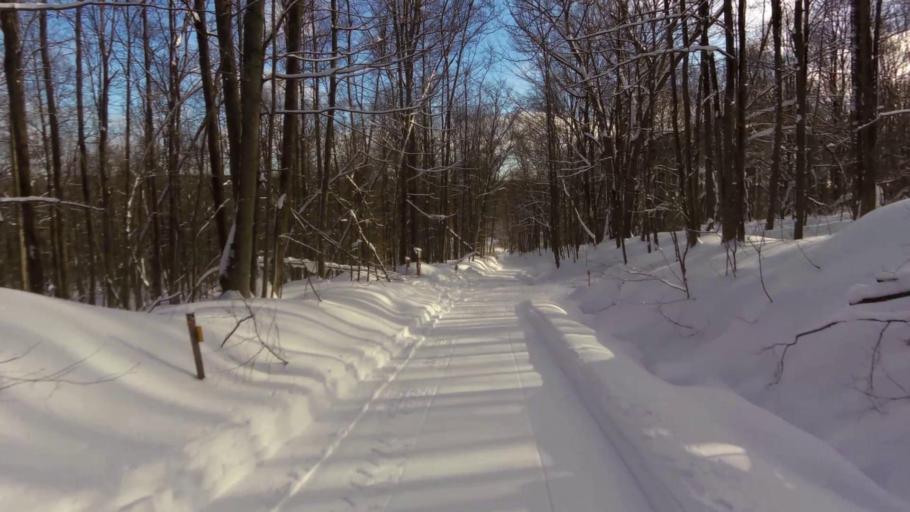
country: US
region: New York
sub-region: Chautauqua County
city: Falconer
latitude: 42.2443
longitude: -79.1491
